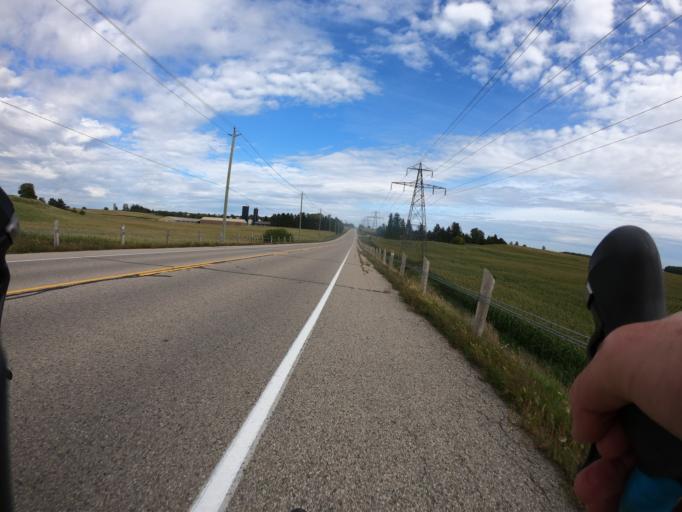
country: CA
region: Ontario
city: Waterloo
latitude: 43.4322
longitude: -80.6458
